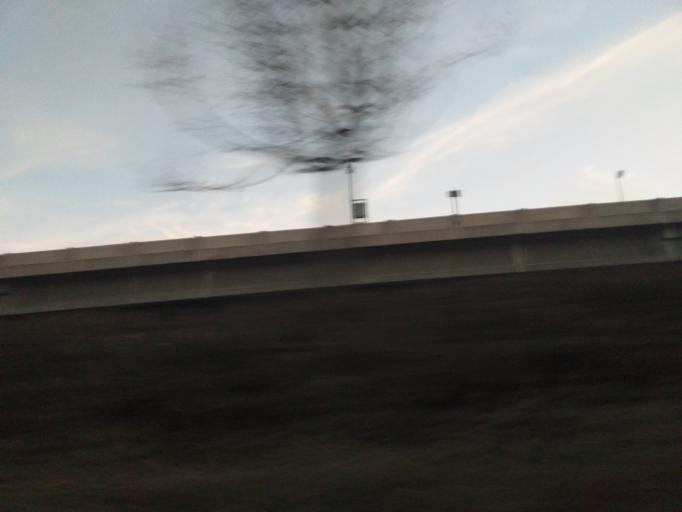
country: TR
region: Ankara
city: Ankara
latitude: 39.9551
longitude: 32.8245
